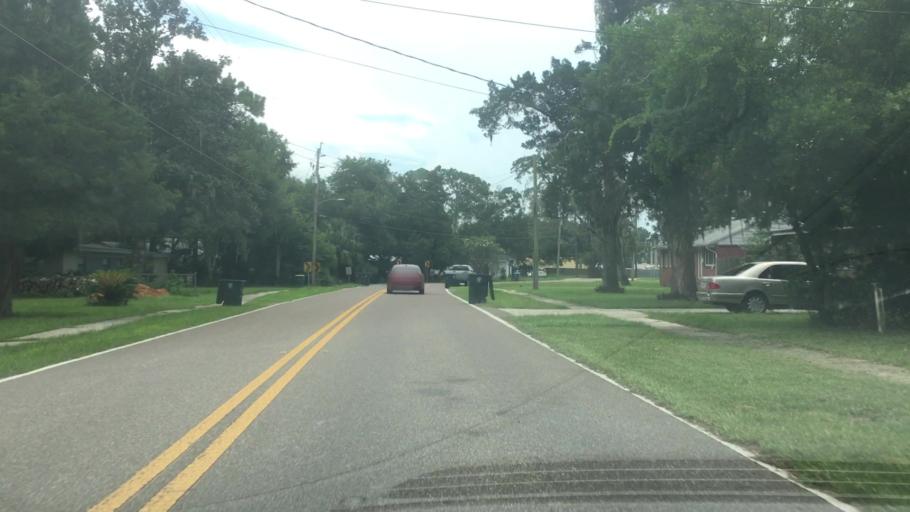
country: US
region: Florida
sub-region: Duval County
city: Jacksonville
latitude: 30.2892
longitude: -81.5484
